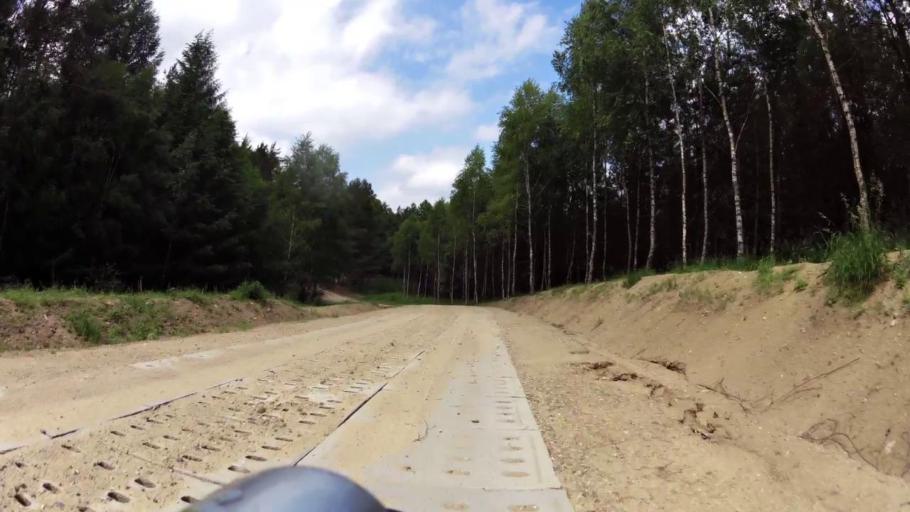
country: PL
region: West Pomeranian Voivodeship
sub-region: Powiat szczecinecki
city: Bialy Bor
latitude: 53.9560
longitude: 16.7574
